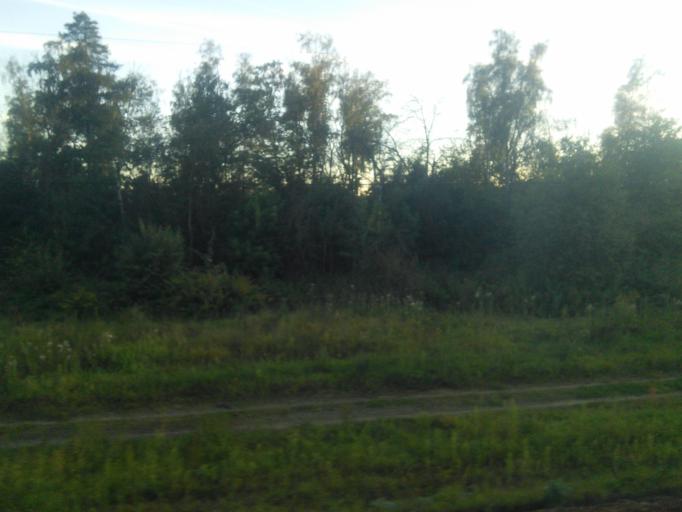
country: RU
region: Moskovskaya
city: Kupavna
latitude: 55.7417
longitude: 38.1618
